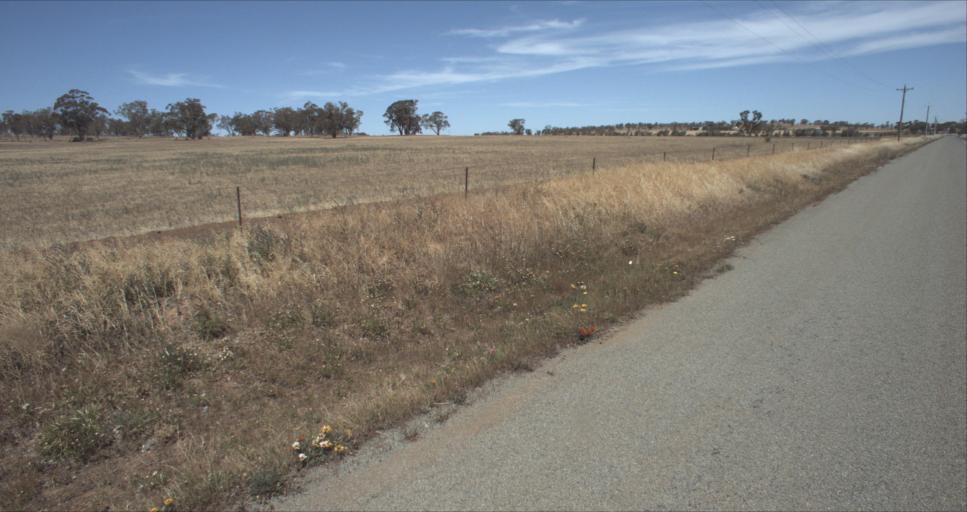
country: AU
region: New South Wales
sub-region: Leeton
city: Leeton
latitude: -34.6103
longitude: 146.4346
